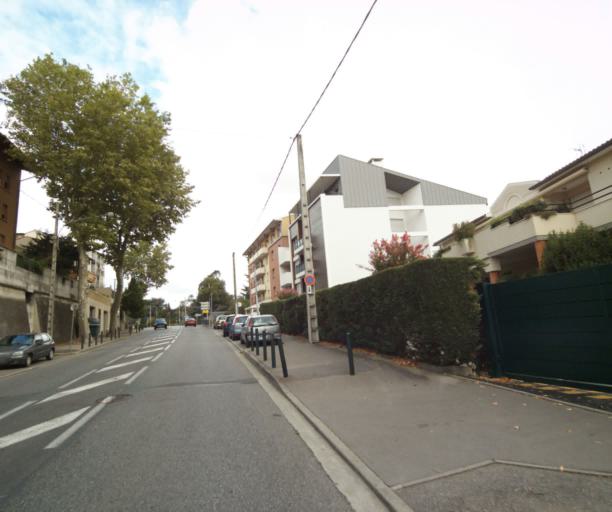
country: FR
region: Midi-Pyrenees
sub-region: Departement de la Haute-Garonne
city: Balma
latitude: 43.6001
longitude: 1.4778
